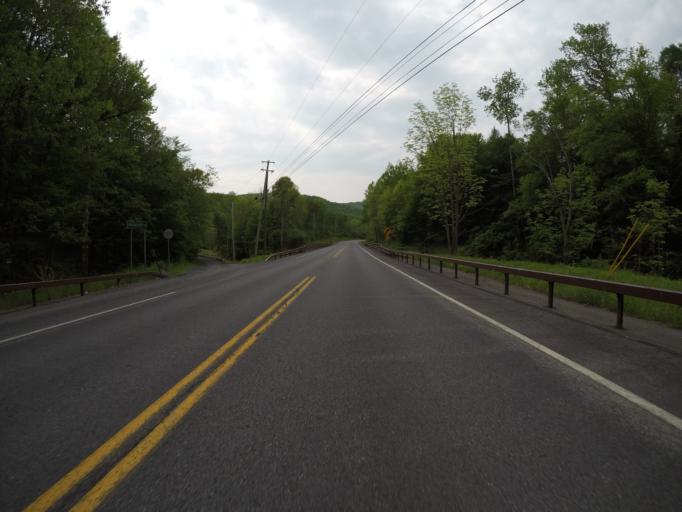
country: US
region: New York
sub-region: Sullivan County
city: Livingston Manor
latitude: 42.0189
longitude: -74.8915
